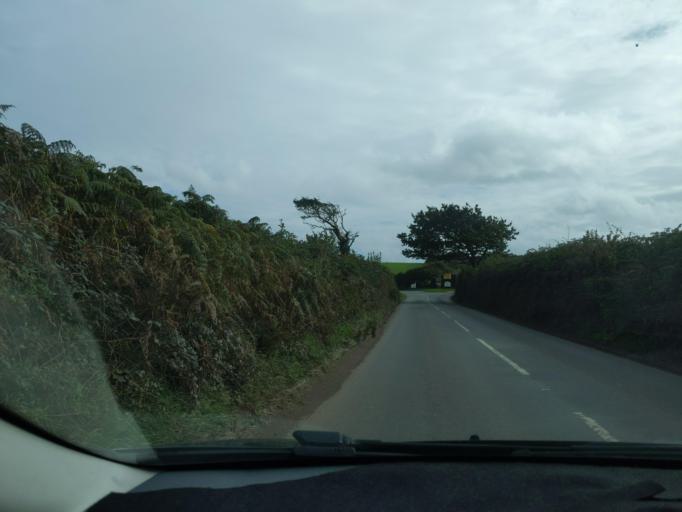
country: GB
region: England
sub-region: Cornwall
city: Mevagissey
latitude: 50.2501
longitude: -4.8204
